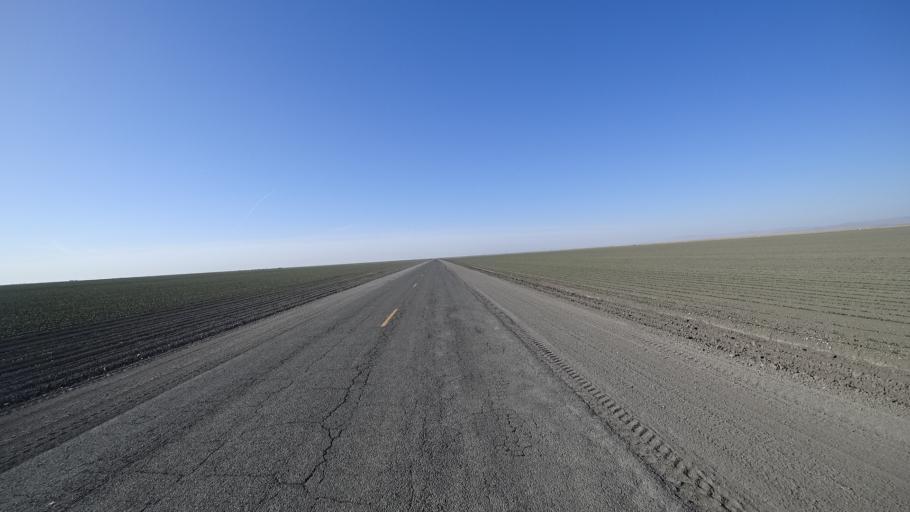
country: US
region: California
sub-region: Kings County
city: Stratford
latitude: 36.0918
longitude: -119.7979
